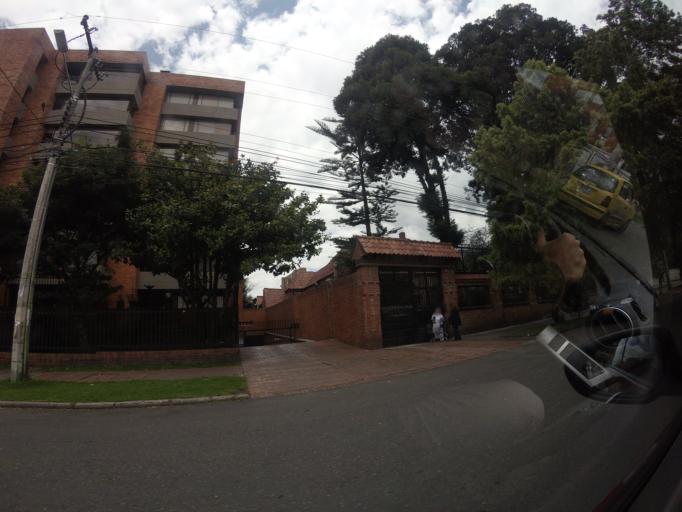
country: CO
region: Bogota D.C.
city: Barrio San Luis
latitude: 4.6610
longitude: -74.0582
